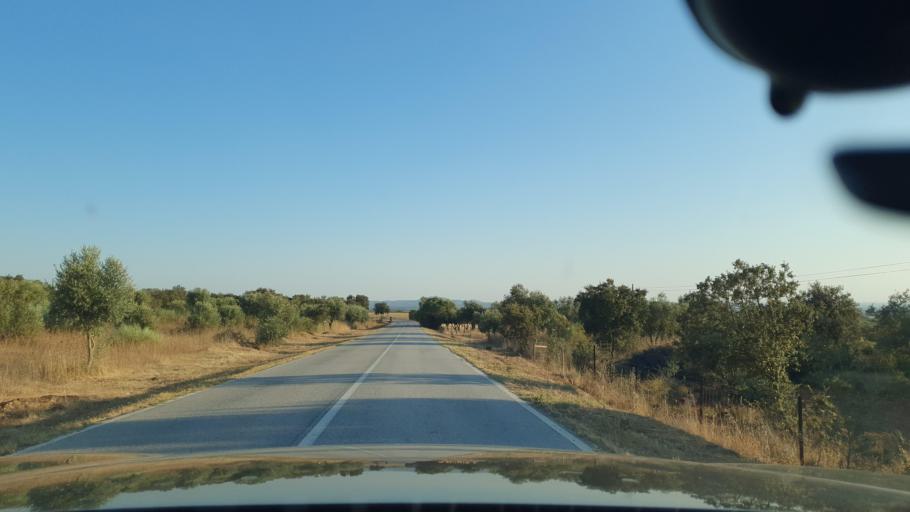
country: PT
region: Evora
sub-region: Estremoz
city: Estremoz
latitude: 38.9054
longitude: -7.6674
